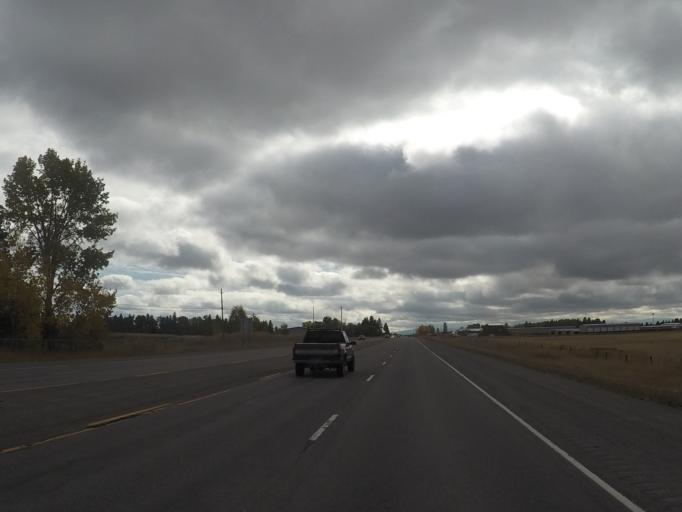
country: US
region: Montana
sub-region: Flathead County
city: Columbia Falls
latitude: 48.3664
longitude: -114.2411
